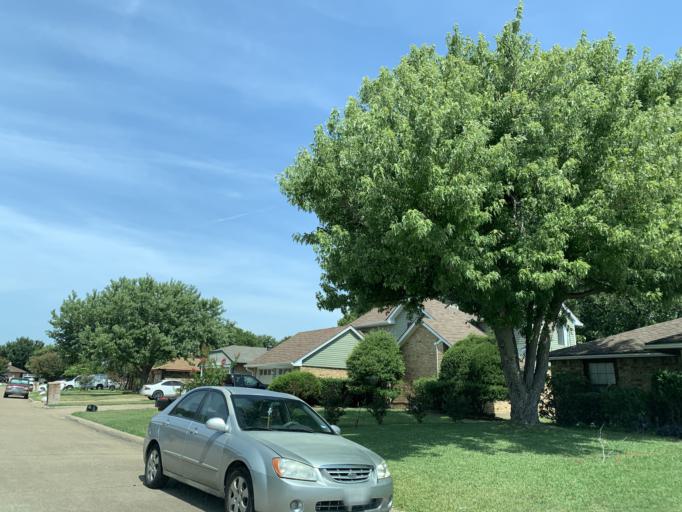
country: US
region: Texas
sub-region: Dallas County
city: Grand Prairie
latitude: 32.6668
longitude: -97.0394
